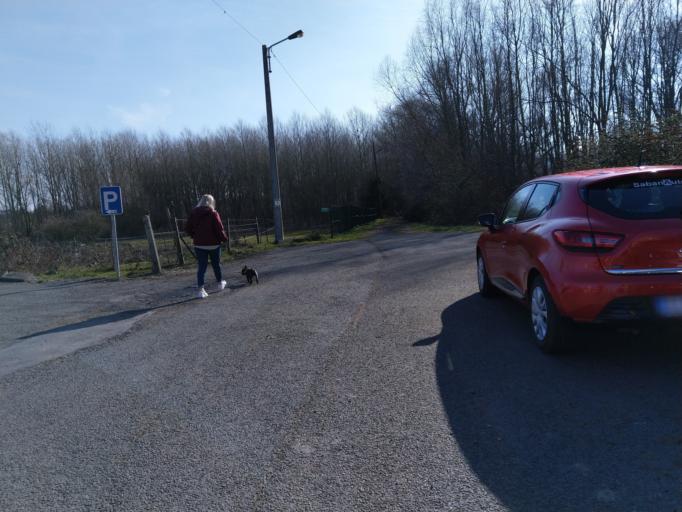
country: BE
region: Wallonia
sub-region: Province du Hainaut
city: Mons
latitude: 50.4465
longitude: 3.9367
